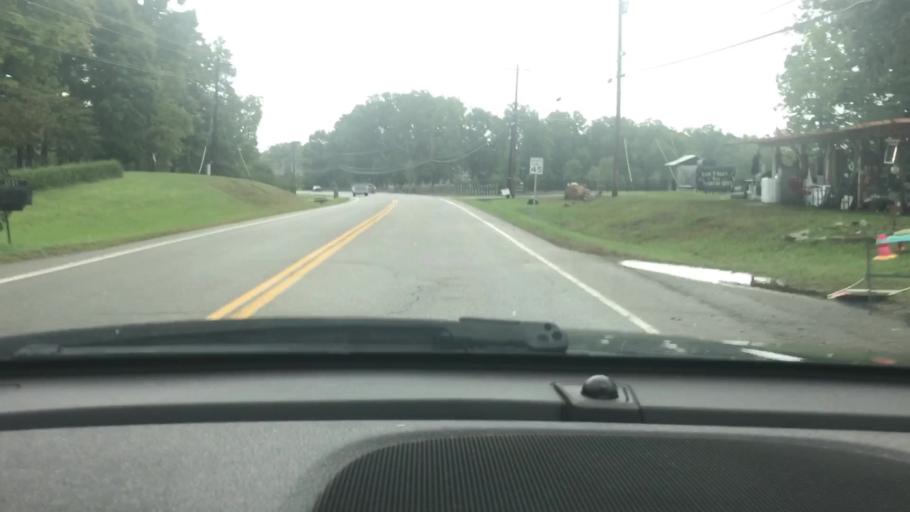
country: US
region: Tennessee
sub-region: Dickson County
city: White Bluff
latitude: 36.1050
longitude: -87.1835
